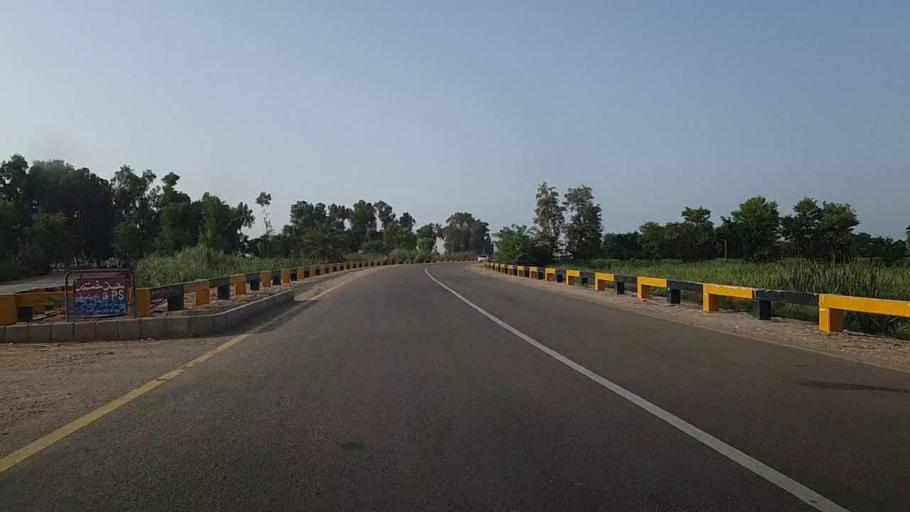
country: PK
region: Sindh
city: Naushahro Firoz
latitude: 26.7899
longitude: 68.1442
